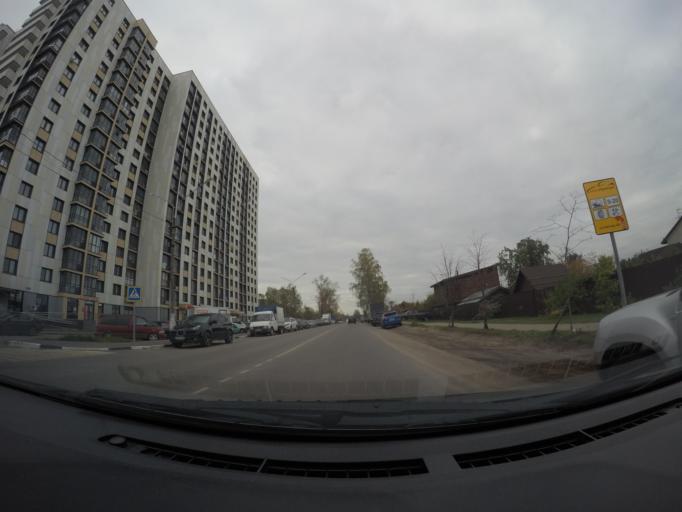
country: RU
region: Moskovskaya
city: Staraya Kupavna
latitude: 55.8021
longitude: 38.1823
